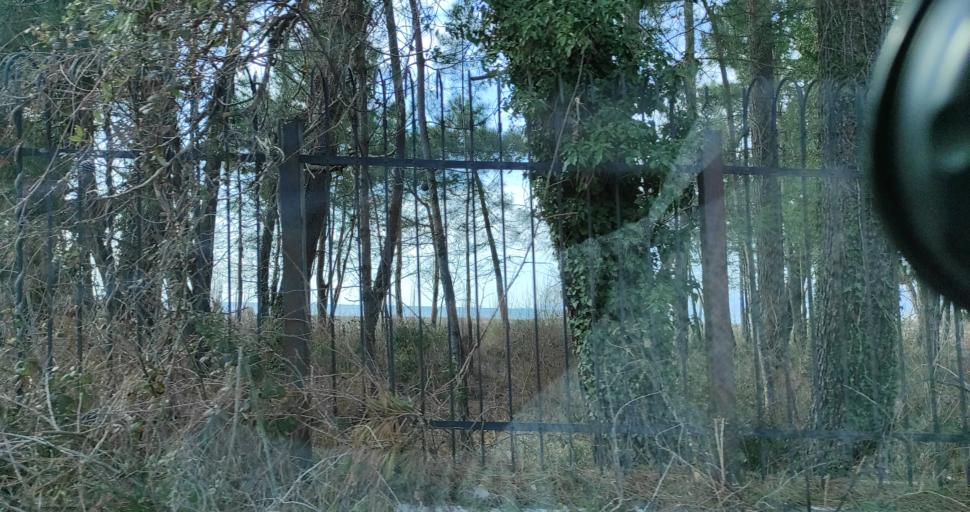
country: AL
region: Lezhe
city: Shengjin
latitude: 41.7802
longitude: 19.6036
